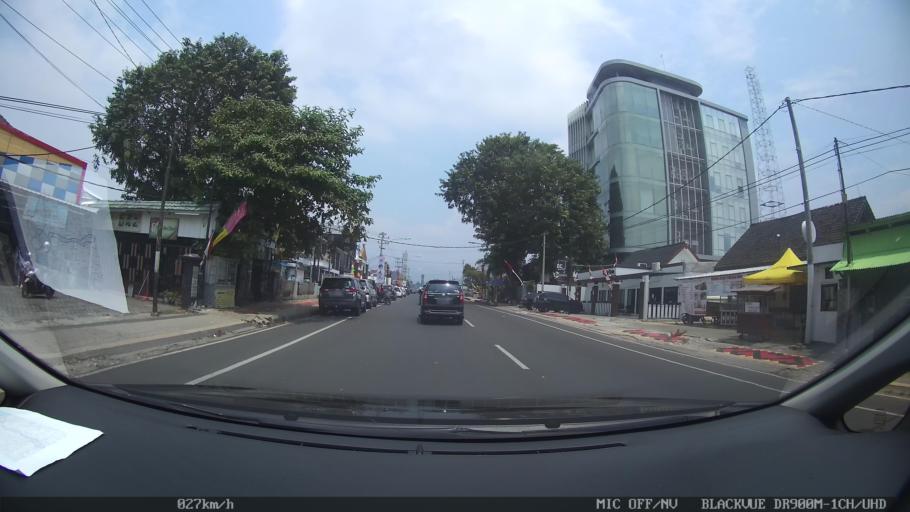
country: ID
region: Lampung
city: Bandarlampung
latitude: -5.4297
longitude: 105.2694
